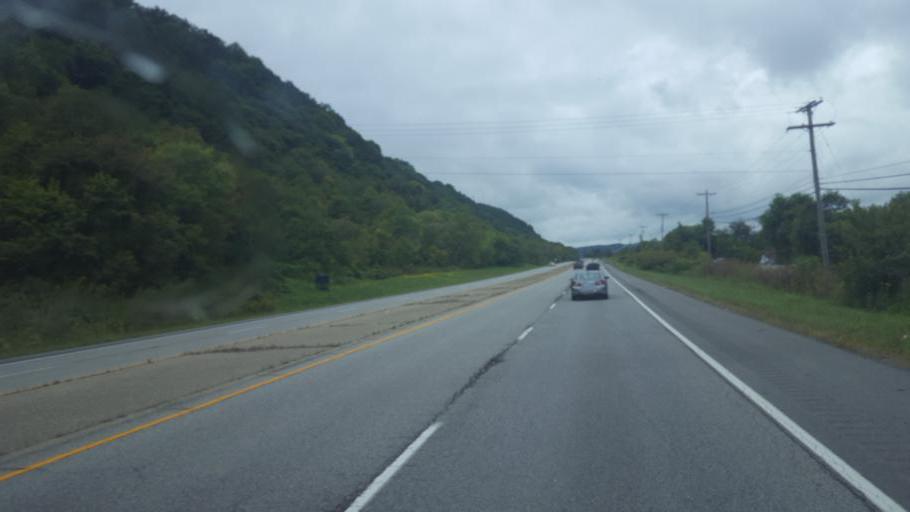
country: US
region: Kentucky
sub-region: Greenup County
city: South Shore
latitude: 38.7212
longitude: -82.9772
